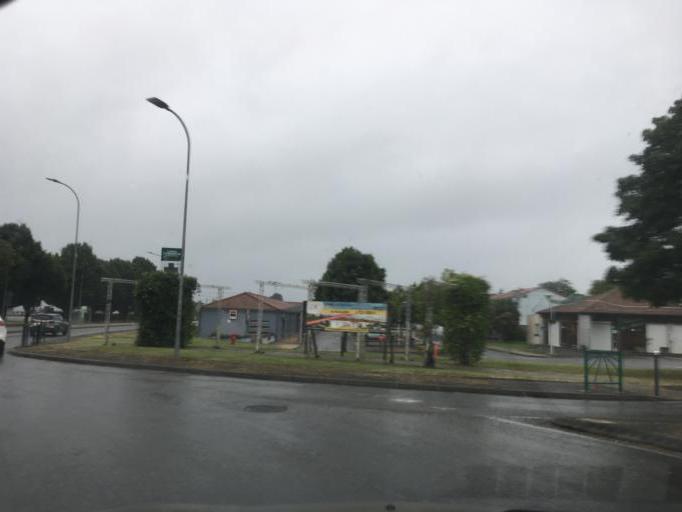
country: FR
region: Midi-Pyrenees
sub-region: Departement des Hautes-Pyrenees
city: Bazet
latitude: 43.2902
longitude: 0.0693
